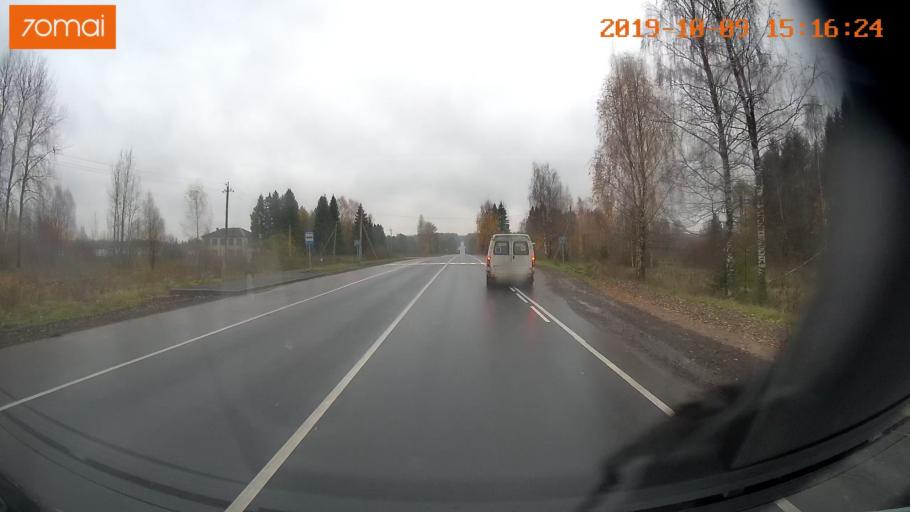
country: RU
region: Kostroma
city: Susanino
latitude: 58.1106
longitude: 41.5860
